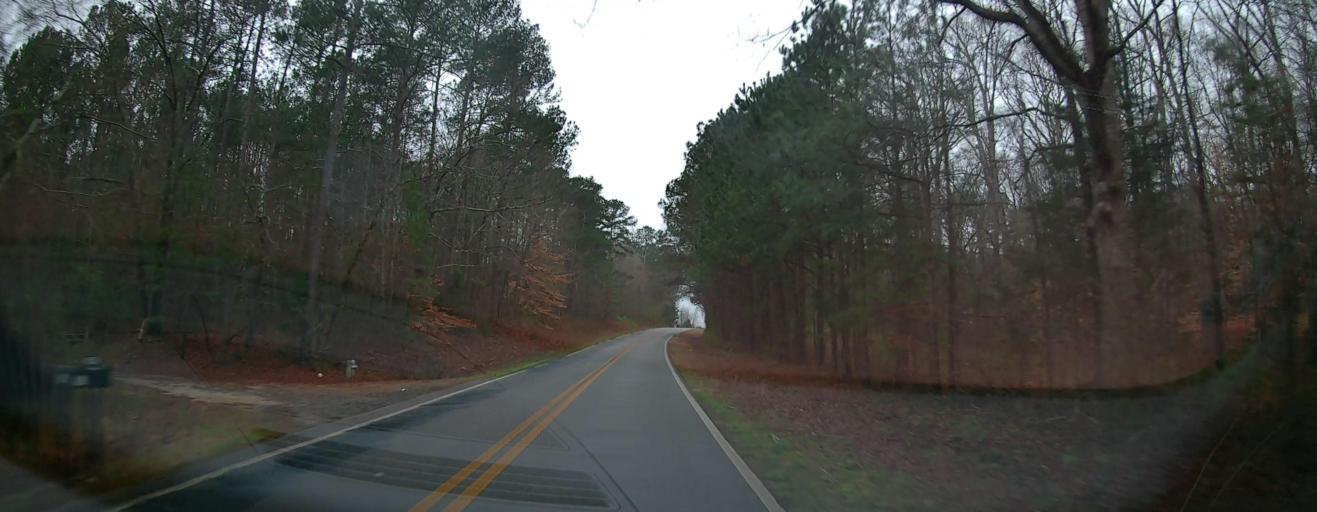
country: US
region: Georgia
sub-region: Monroe County
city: Forsyth
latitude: 33.1112
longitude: -84.0373
